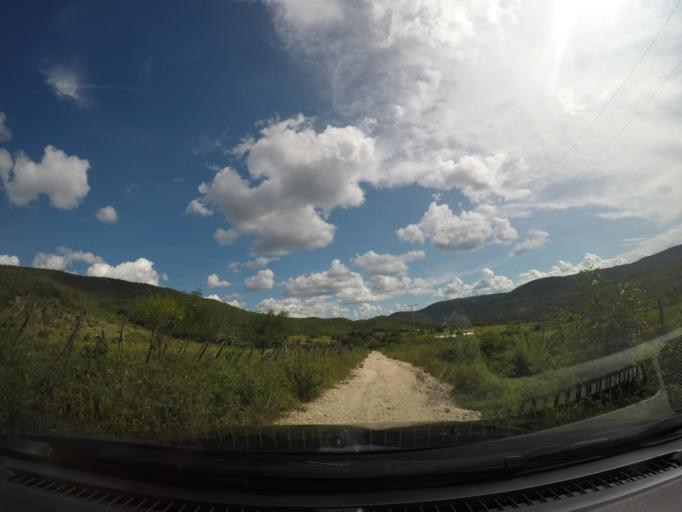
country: BR
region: Bahia
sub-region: Barra Da Estiva
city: Barra da Estiva
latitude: -13.1265
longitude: -41.5942
